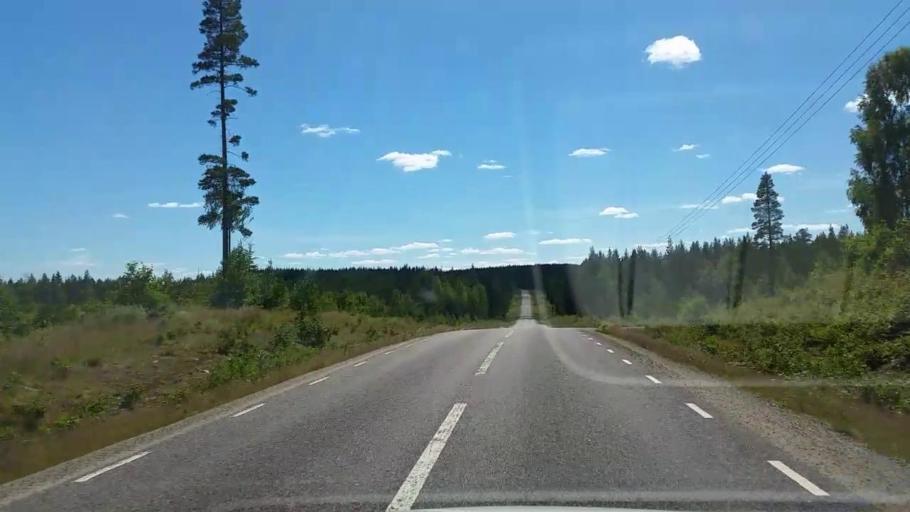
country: SE
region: Gaevleborg
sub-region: Ovanakers Kommun
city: Edsbyn
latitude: 61.5380
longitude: 15.6813
